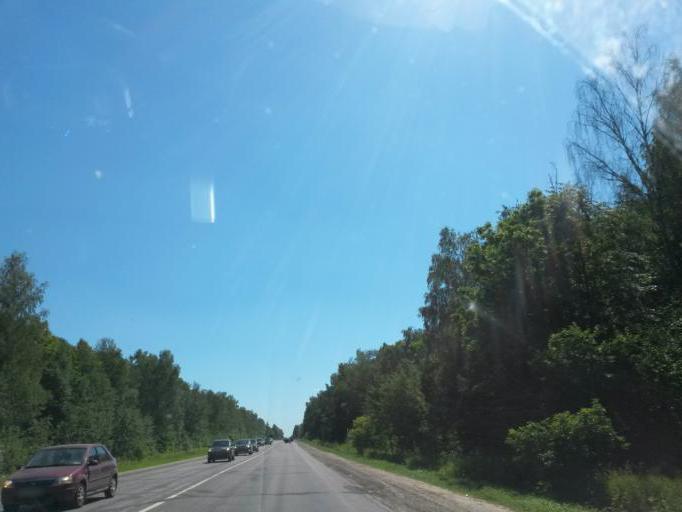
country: RU
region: Moskovskaya
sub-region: Chekhovskiy Rayon
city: Chekhov
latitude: 55.0869
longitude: 37.4414
